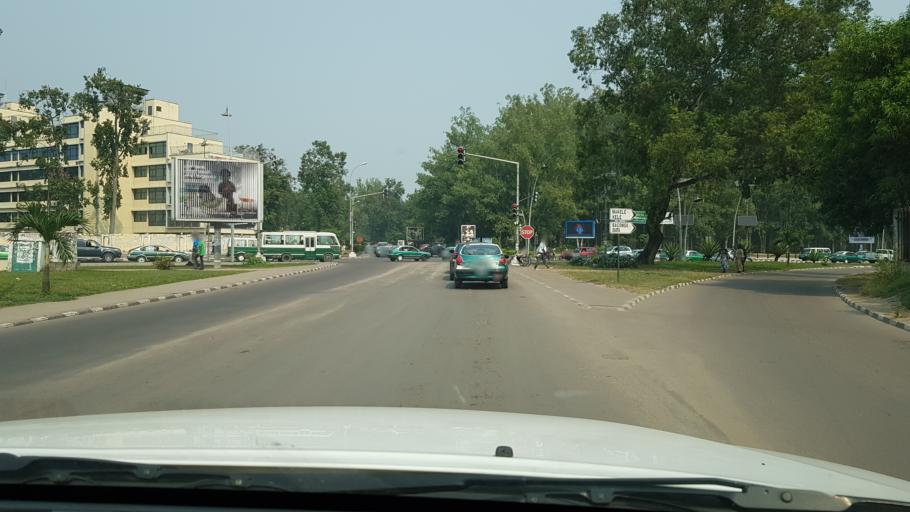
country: CG
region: Brazzaville
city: Brazzaville
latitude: -4.2637
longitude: 15.2608
